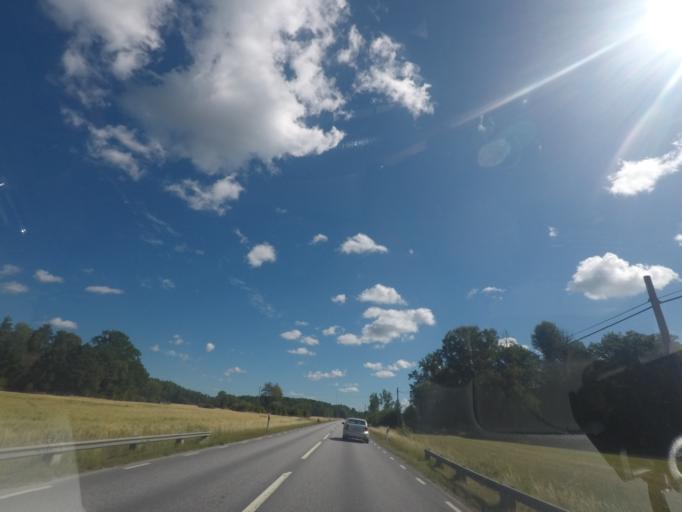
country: SE
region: Stockholm
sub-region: Norrtalje Kommun
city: Skanninge
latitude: 59.8947
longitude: 18.4276
